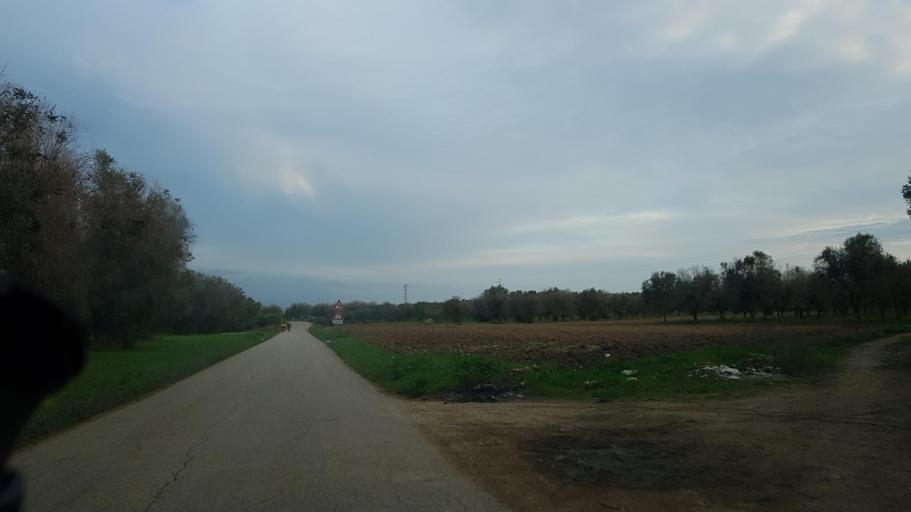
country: IT
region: Apulia
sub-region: Provincia di Brindisi
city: Latiano
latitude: 40.5409
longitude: 17.7393
